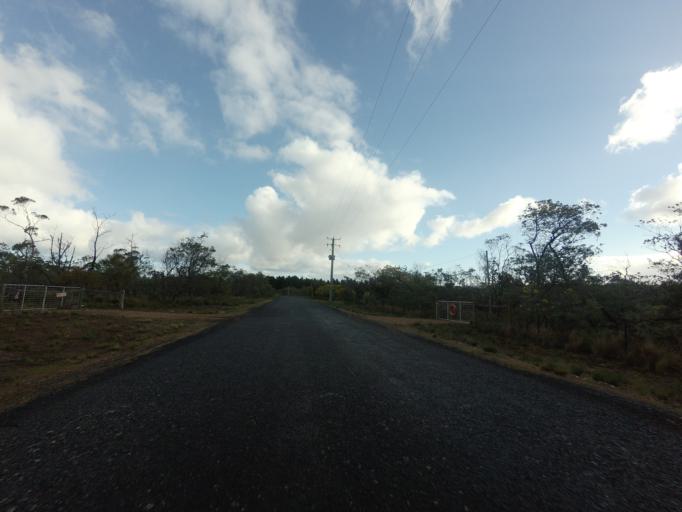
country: AU
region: Tasmania
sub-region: Break O'Day
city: St Helens
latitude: -42.1030
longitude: 148.0728
